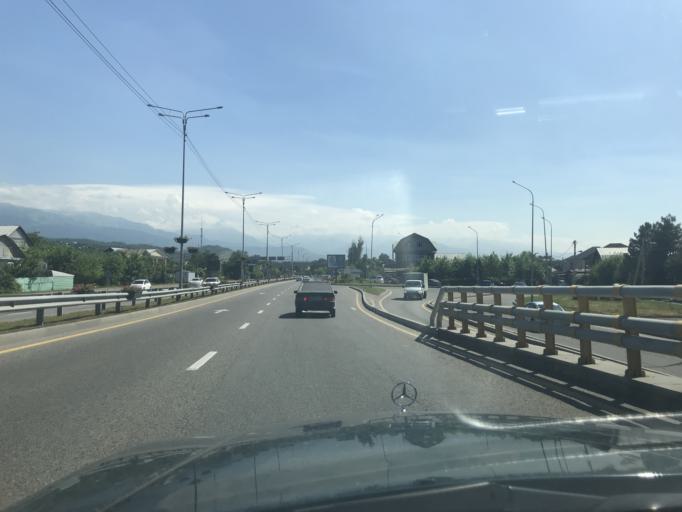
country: KZ
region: Almaty Qalasy
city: Almaty
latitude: 43.2821
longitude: 76.9862
